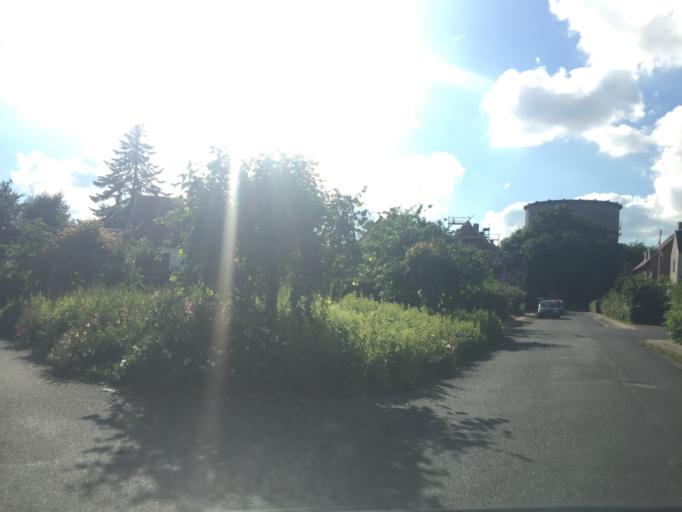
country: DK
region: Capital Region
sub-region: Kobenhavn
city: Vanlose
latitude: 55.6993
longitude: 12.5013
